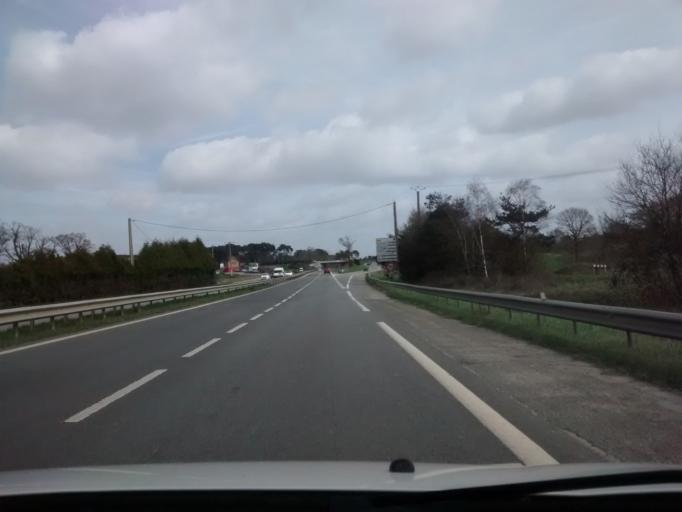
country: FR
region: Brittany
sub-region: Departement d'Ille-et-Vilaine
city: Saint-Jacques-de-la-Lande
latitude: 48.0520
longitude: -1.7436
